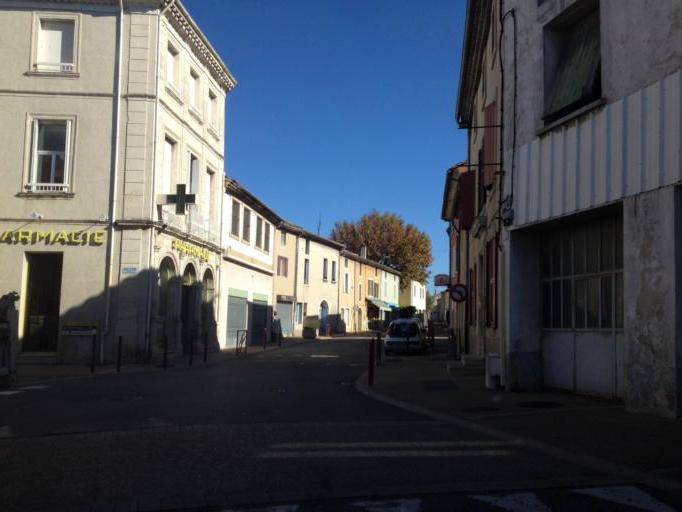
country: FR
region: Provence-Alpes-Cote d'Azur
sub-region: Departement du Vaucluse
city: Jonquieres
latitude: 44.1153
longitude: 4.8987
